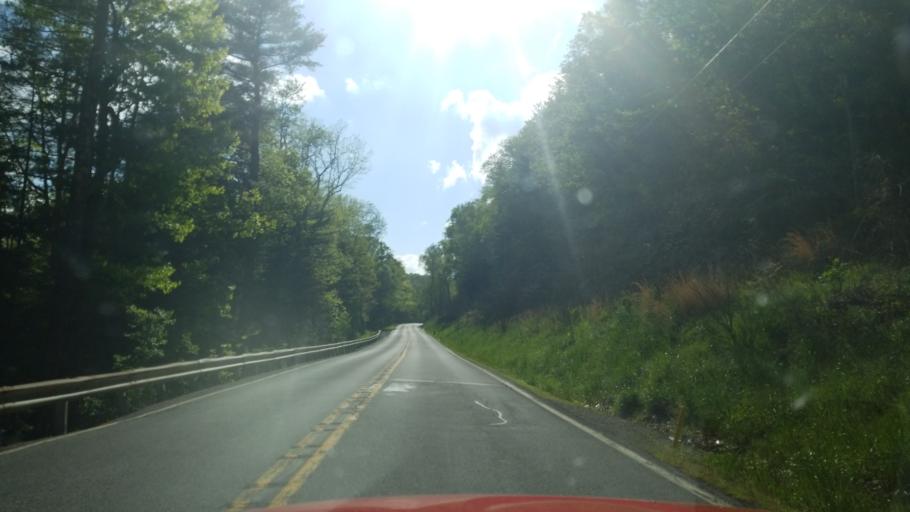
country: US
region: Pennsylvania
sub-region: Clearfield County
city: Hyde
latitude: 40.9705
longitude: -78.4196
